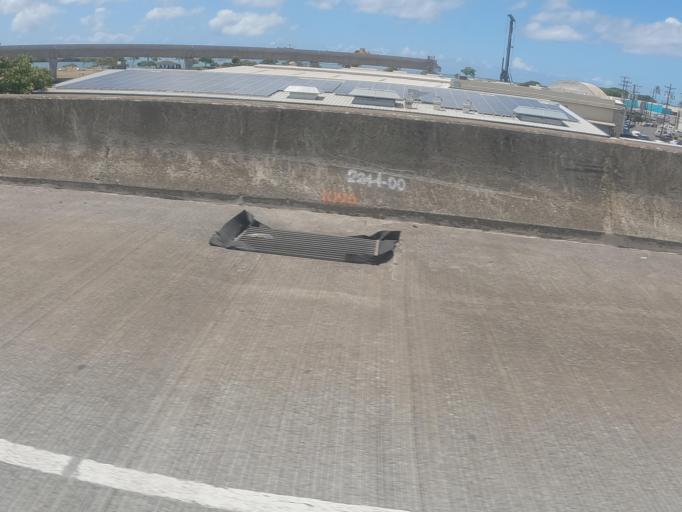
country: US
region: Hawaii
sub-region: Honolulu County
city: Halawa Heights
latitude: 21.3344
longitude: -157.8979
